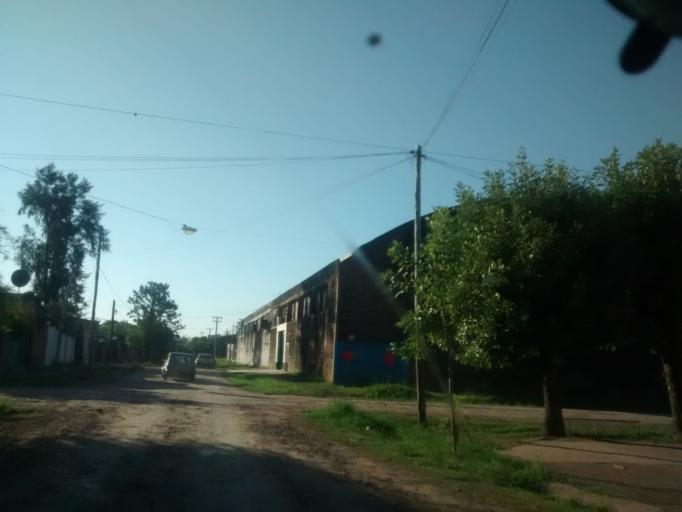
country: AR
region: Chaco
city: Resistencia
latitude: -27.4499
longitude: -59.0099
